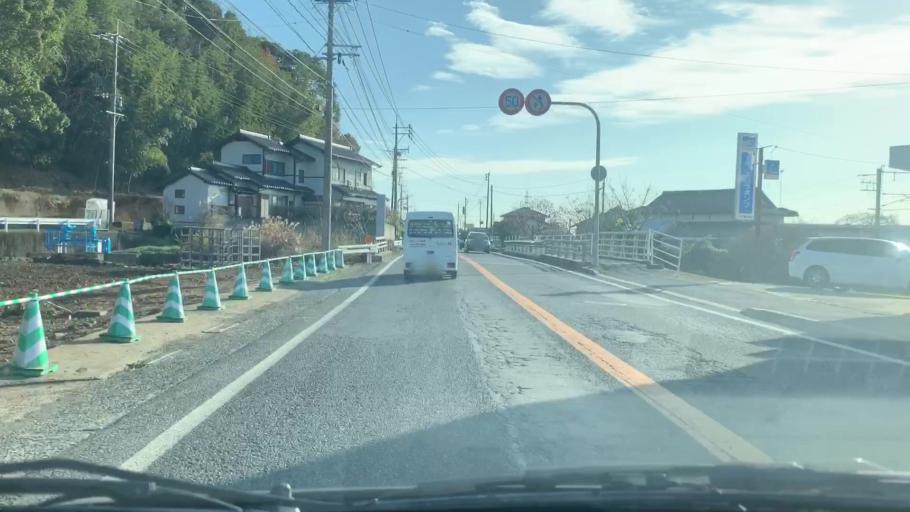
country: JP
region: Saga Prefecture
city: Takeocho-takeo
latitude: 33.2156
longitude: 130.0899
